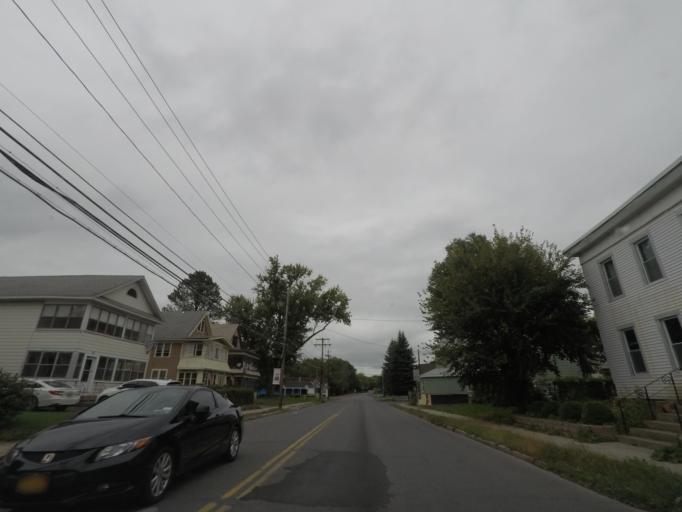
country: US
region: New York
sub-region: Rensselaer County
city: Rensselaer
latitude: 42.6592
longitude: -73.7254
